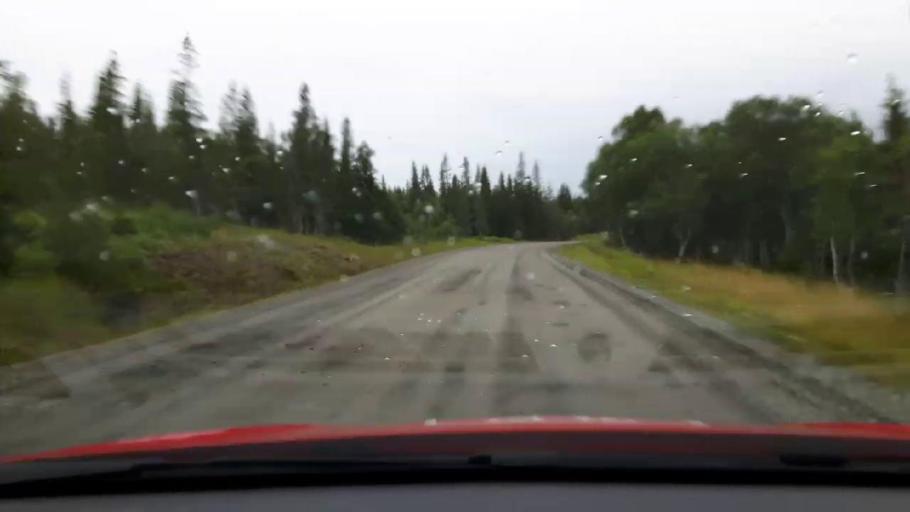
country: NO
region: Nord-Trondelag
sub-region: Meraker
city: Meraker
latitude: 63.5466
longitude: 12.3783
